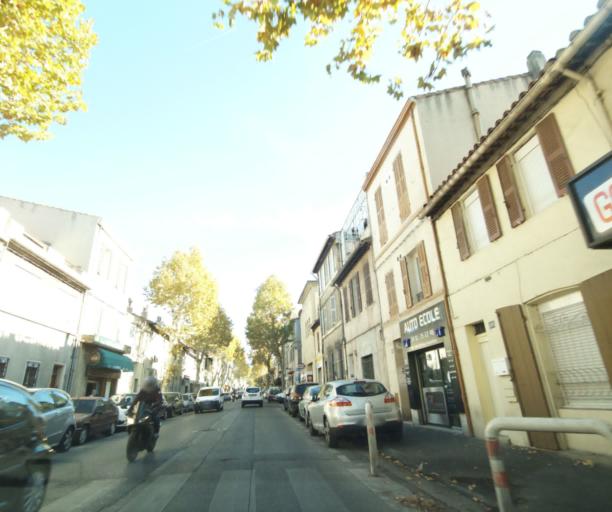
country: FR
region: Provence-Alpes-Cote d'Azur
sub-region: Departement des Bouches-du-Rhone
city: Marseille 11
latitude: 43.2882
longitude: 5.4633
